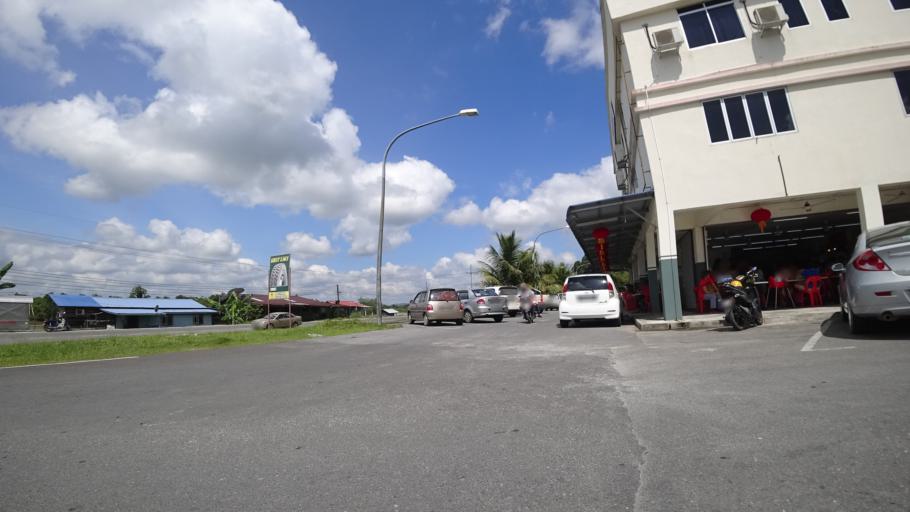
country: MY
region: Sarawak
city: Limbang
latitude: 4.7597
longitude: 115.0056
